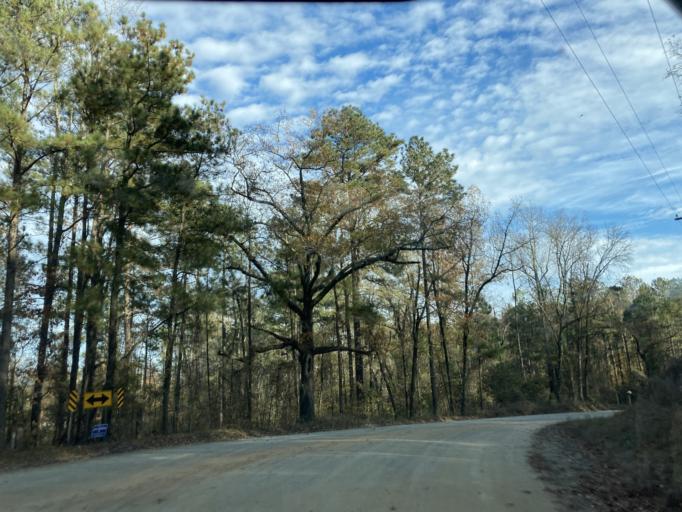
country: US
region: Georgia
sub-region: Jones County
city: Gray
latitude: 32.9120
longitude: -83.4896
